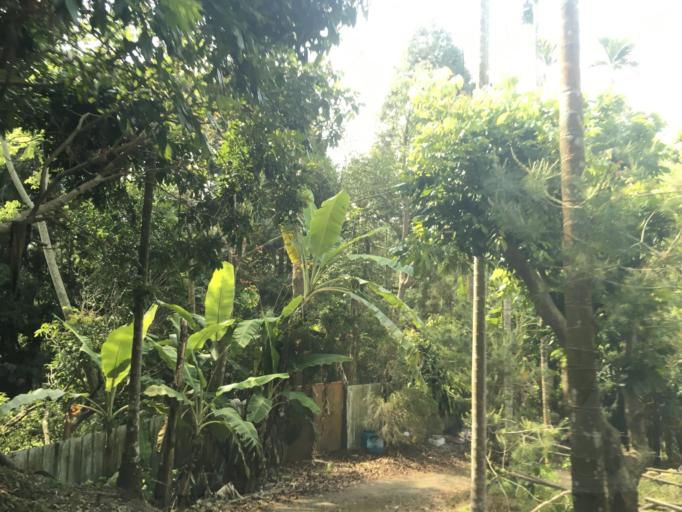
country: TW
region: Taiwan
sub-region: Taichung City
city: Taichung
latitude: 24.1326
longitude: 120.8246
